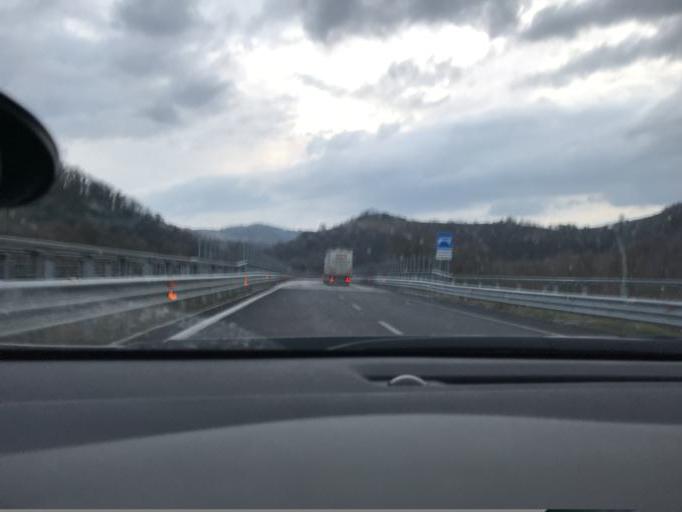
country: IT
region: Umbria
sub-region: Provincia di Perugia
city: Valfabbrica
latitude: 43.1535
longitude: 12.5836
